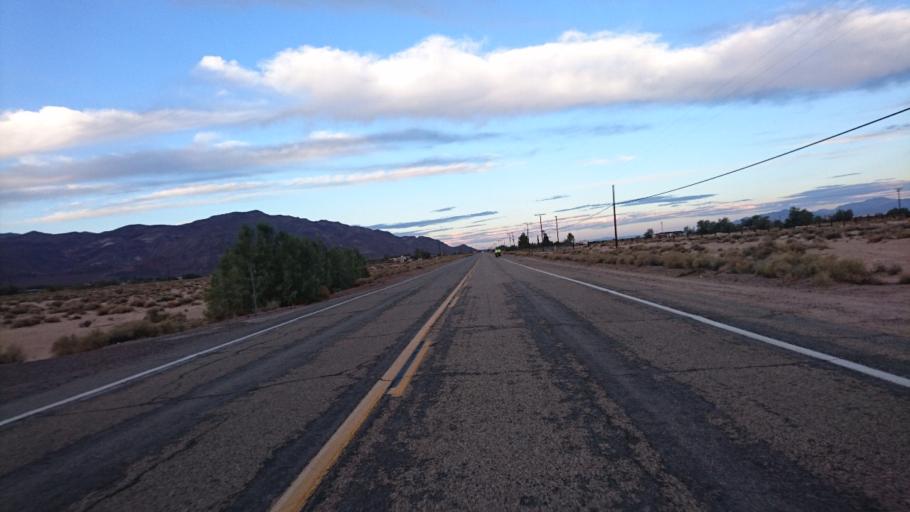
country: US
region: California
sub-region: San Bernardino County
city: Barstow
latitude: 34.8166
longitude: -116.6276
